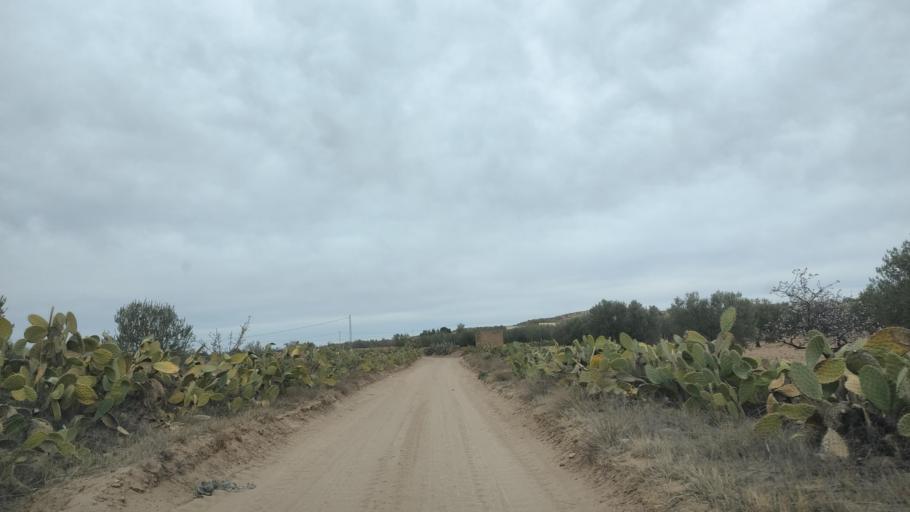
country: TN
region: Al Qasrayn
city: Kasserine
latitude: 35.2447
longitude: 8.9181
